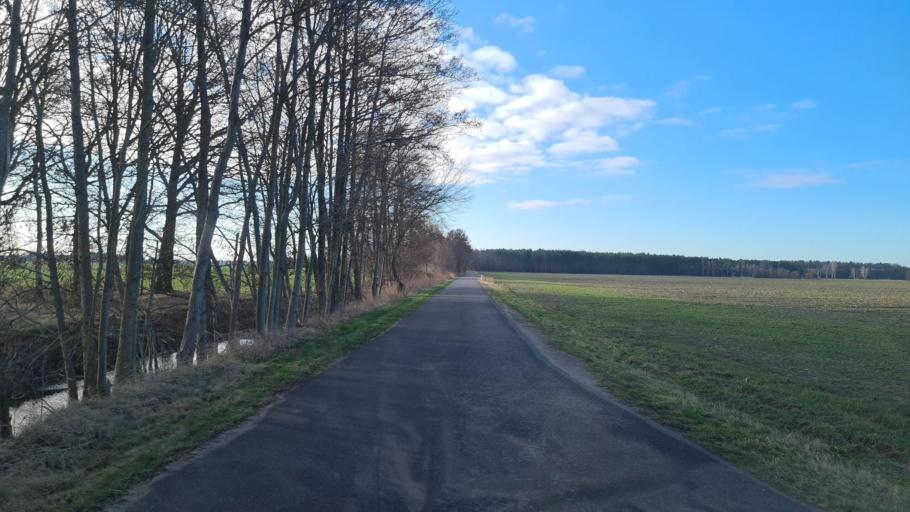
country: DE
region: Brandenburg
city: Herzberg
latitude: 51.6963
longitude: 13.2061
